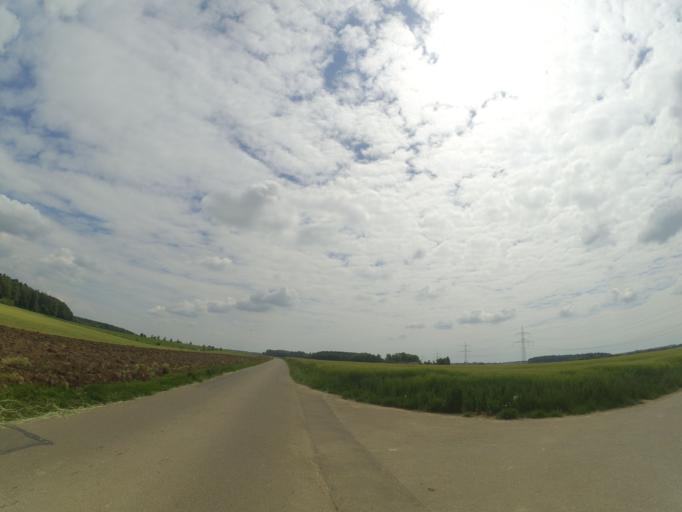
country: DE
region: Baden-Wuerttemberg
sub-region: Tuebingen Region
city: Blaubeuren
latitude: 48.4293
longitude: 9.7821
